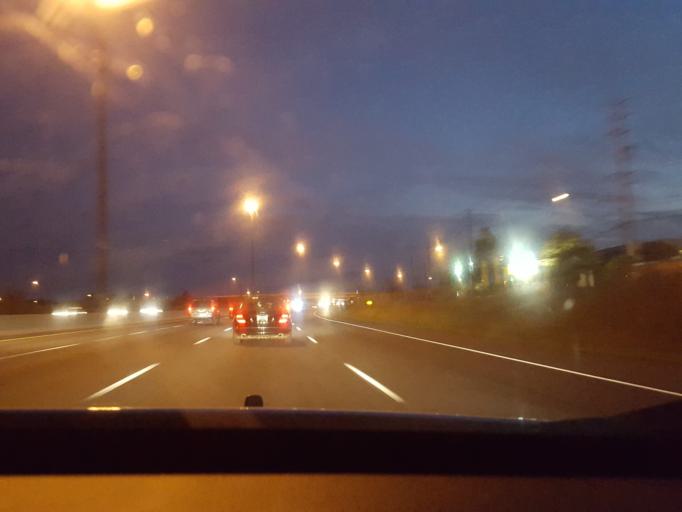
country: CA
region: Ontario
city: Oakville
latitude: 43.4761
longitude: -79.6726
